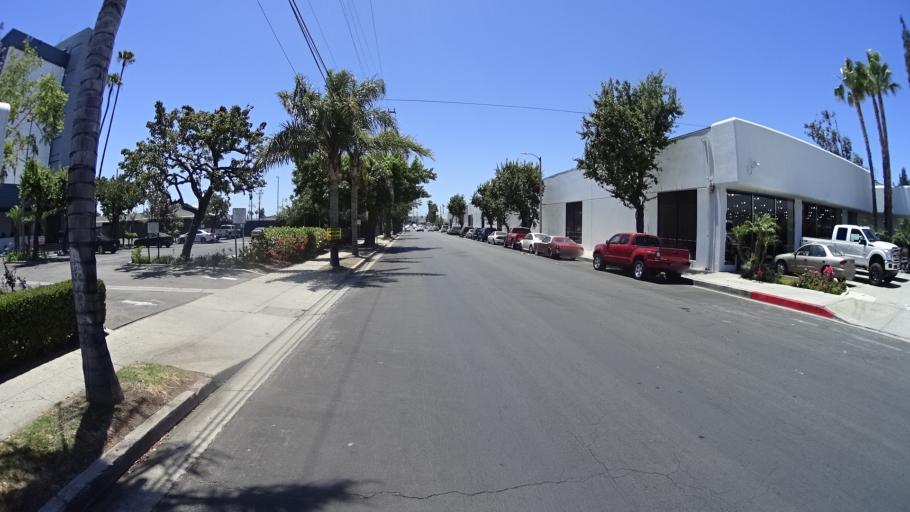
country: US
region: California
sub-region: Los Angeles County
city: Van Nuys
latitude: 34.2206
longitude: -118.4720
